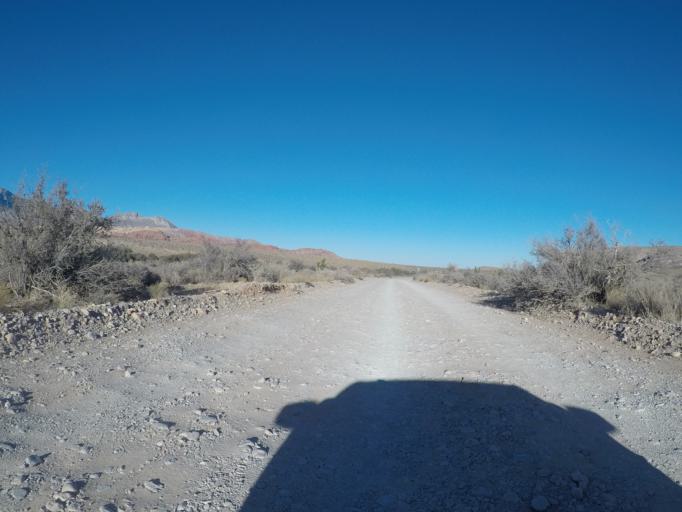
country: US
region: Nevada
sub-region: Clark County
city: Summerlin South
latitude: 36.1163
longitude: -115.4576
